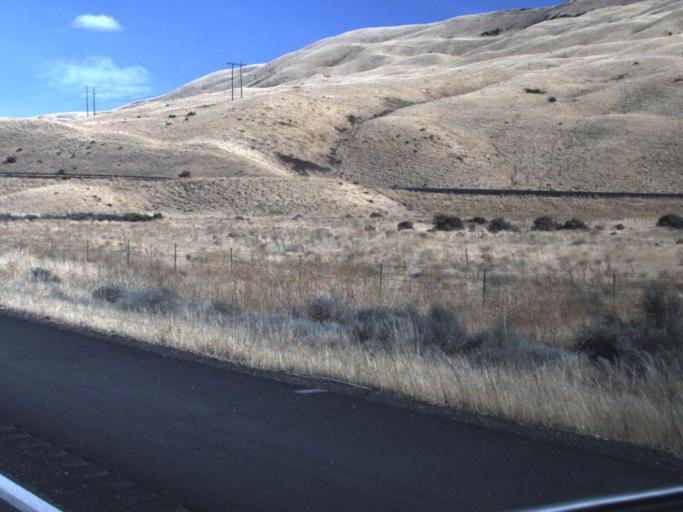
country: US
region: Washington
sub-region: Benton County
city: Benton City
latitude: 46.2476
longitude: -119.6226
